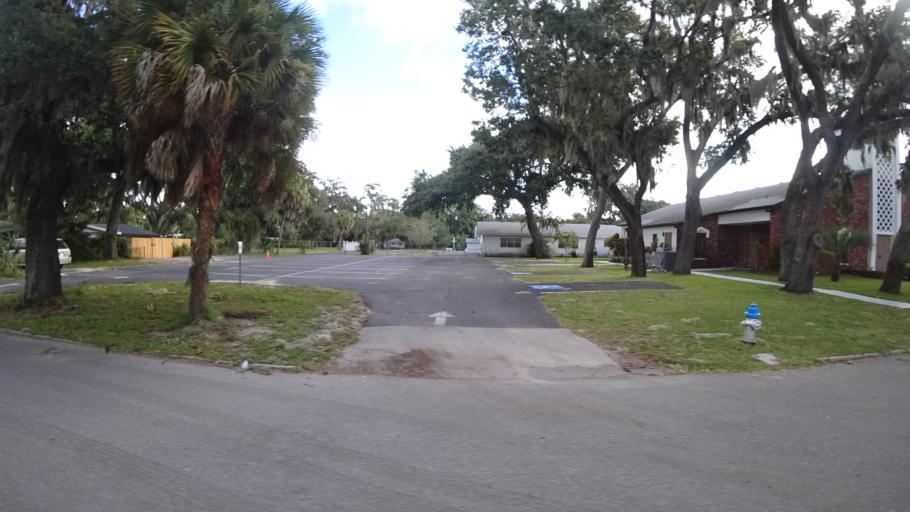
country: US
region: Florida
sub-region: Manatee County
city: Bradenton
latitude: 27.4974
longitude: -82.5479
